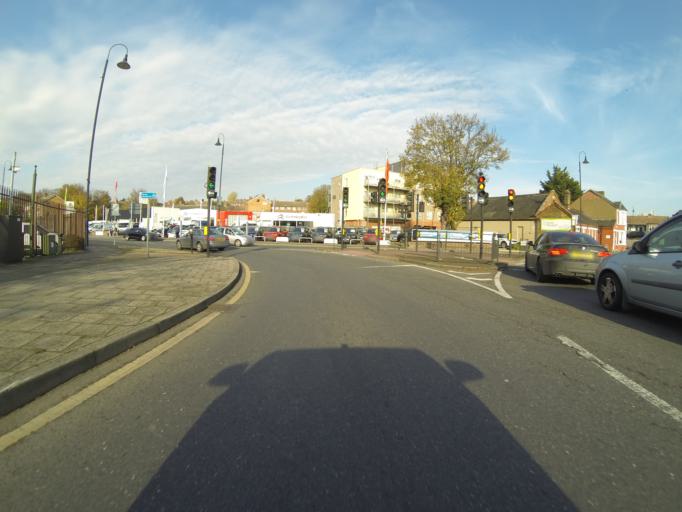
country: GB
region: England
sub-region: Greater London
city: Bexley
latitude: 51.4512
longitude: 0.1770
